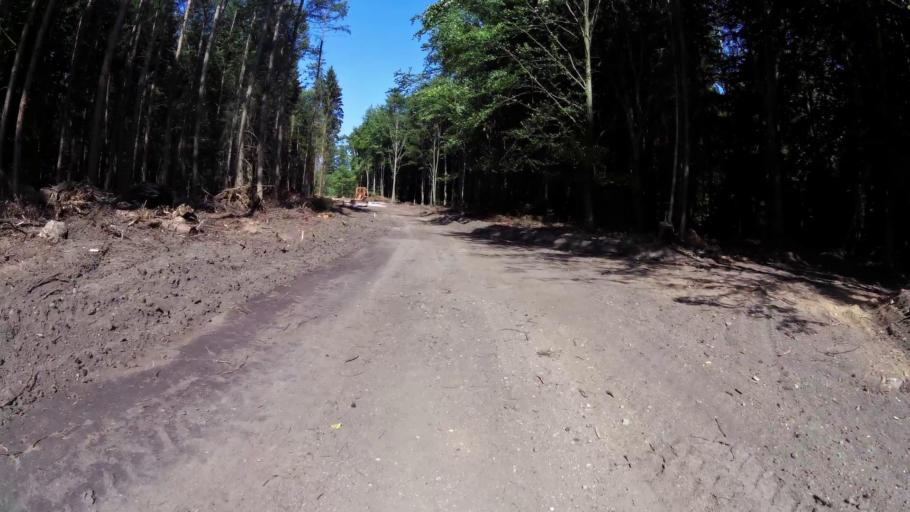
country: PL
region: West Pomeranian Voivodeship
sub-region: Powiat drawski
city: Wierzchowo
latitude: 53.4126
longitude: 16.2317
